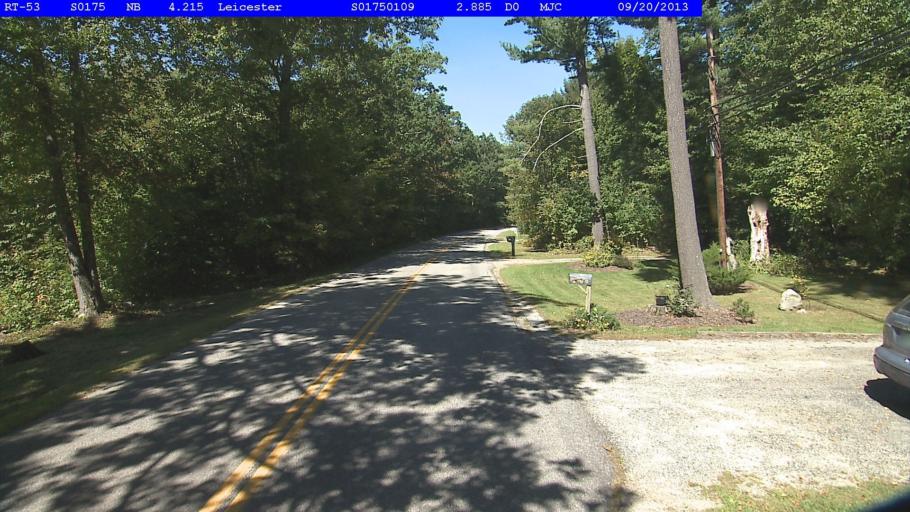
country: US
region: Vermont
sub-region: Rutland County
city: Brandon
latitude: 43.8842
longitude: -73.0641
